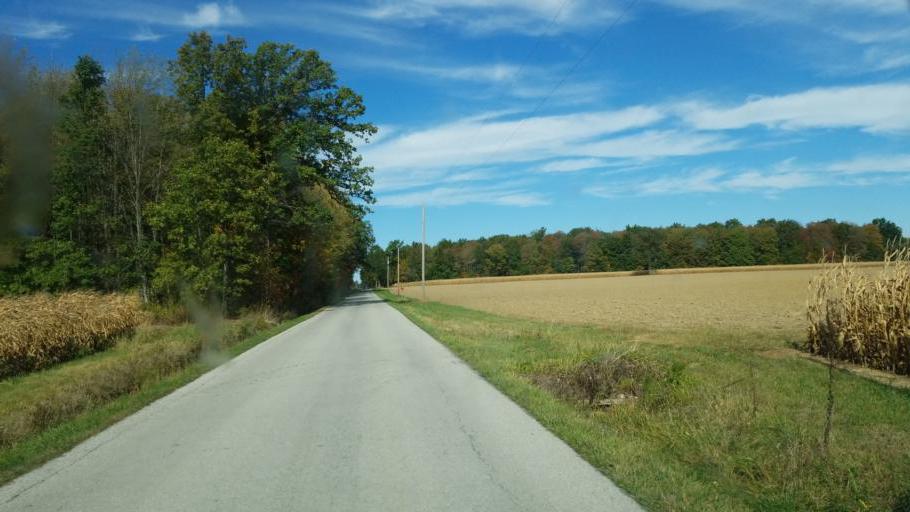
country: US
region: Ohio
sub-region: Huron County
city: Wakeman
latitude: 41.2085
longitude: -82.4591
